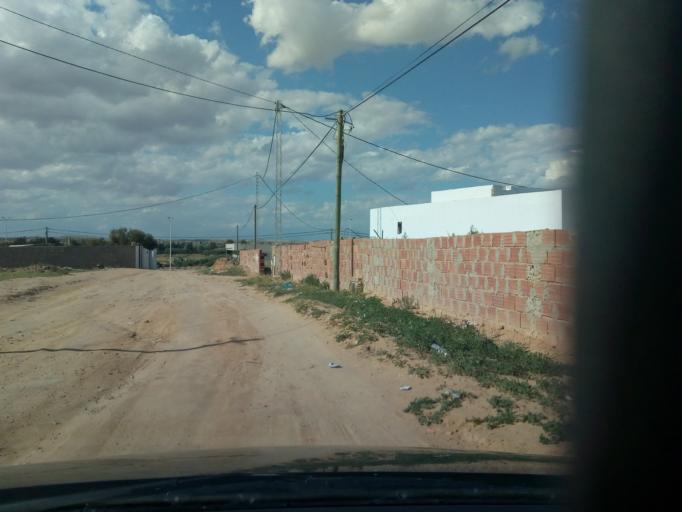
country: TN
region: Safaqis
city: Sfax
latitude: 34.7307
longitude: 10.6004
